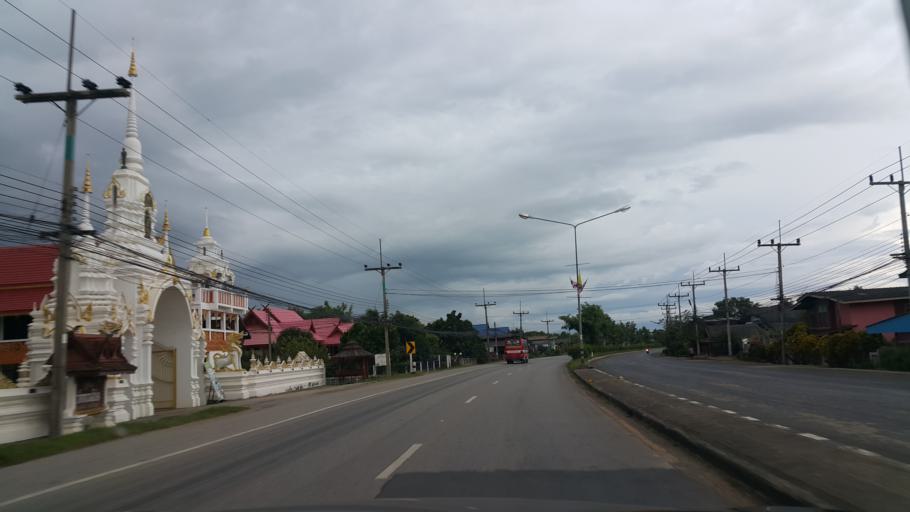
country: TH
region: Phayao
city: Dok Kham Tai
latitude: 19.1524
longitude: 99.9357
